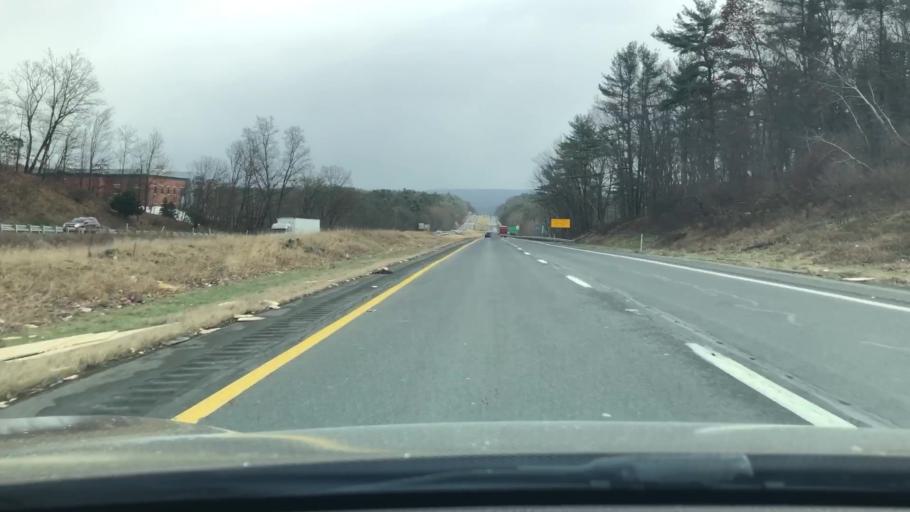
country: US
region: Pennsylvania
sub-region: Monroe County
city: Arlington Heights
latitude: 40.9970
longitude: -75.2675
